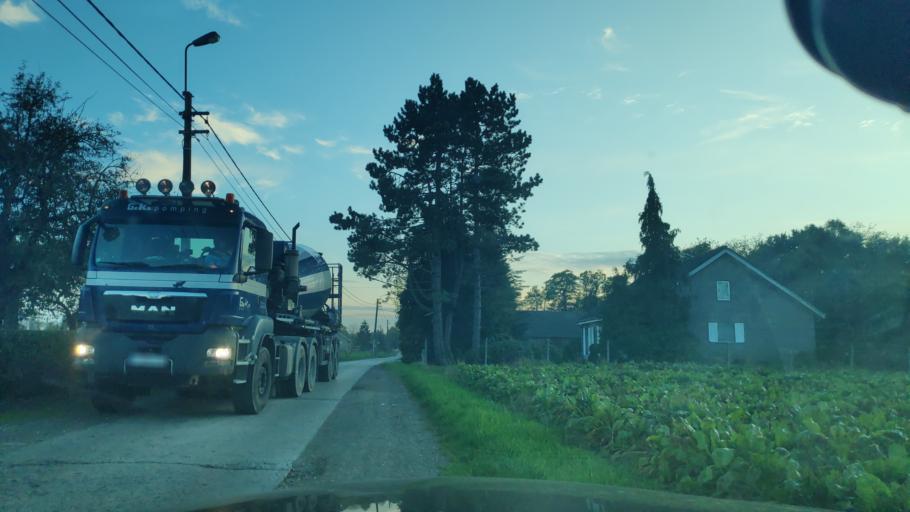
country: BE
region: Flanders
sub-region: Provincie Oost-Vlaanderen
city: Zomergem
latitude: 51.1323
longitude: 3.5055
